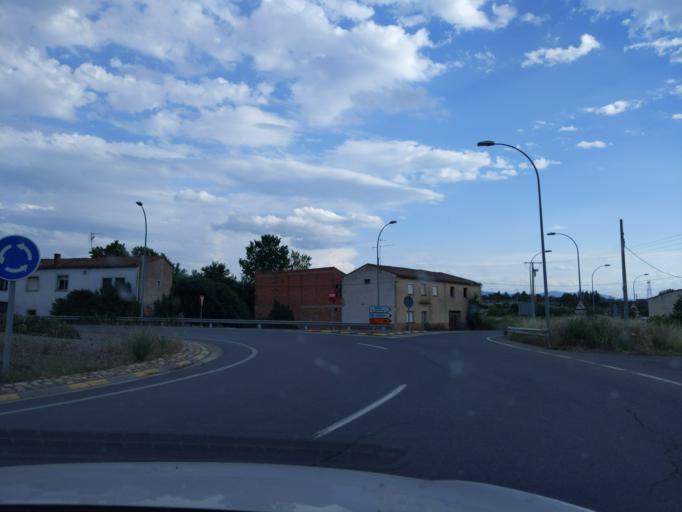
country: ES
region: La Rioja
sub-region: Provincia de La Rioja
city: Villamediana de Iregua
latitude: 42.4235
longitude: -2.4246
